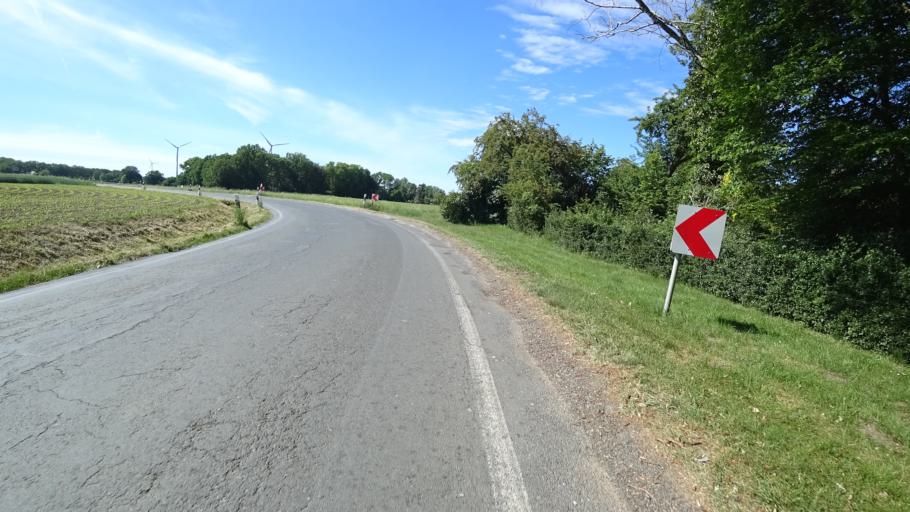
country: DE
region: North Rhine-Westphalia
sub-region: Regierungsbezirk Detmold
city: Rheda-Wiedenbruck
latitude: 51.8237
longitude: 8.2622
